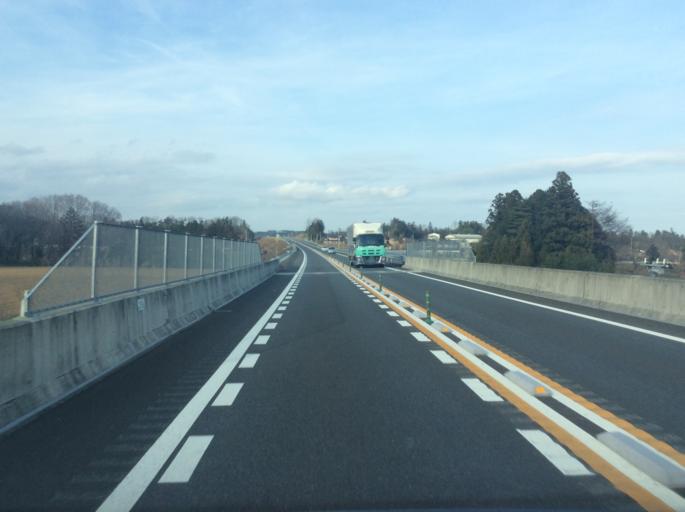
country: JP
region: Fukushima
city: Namie
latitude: 37.5591
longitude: 140.9464
